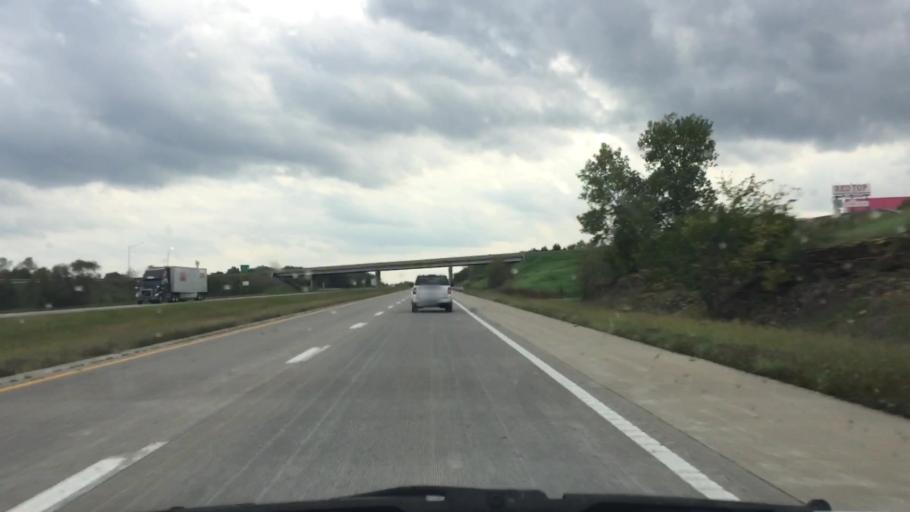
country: US
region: Missouri
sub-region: Clinton County
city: Cameron
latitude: 39.6701
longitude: -94.2353
